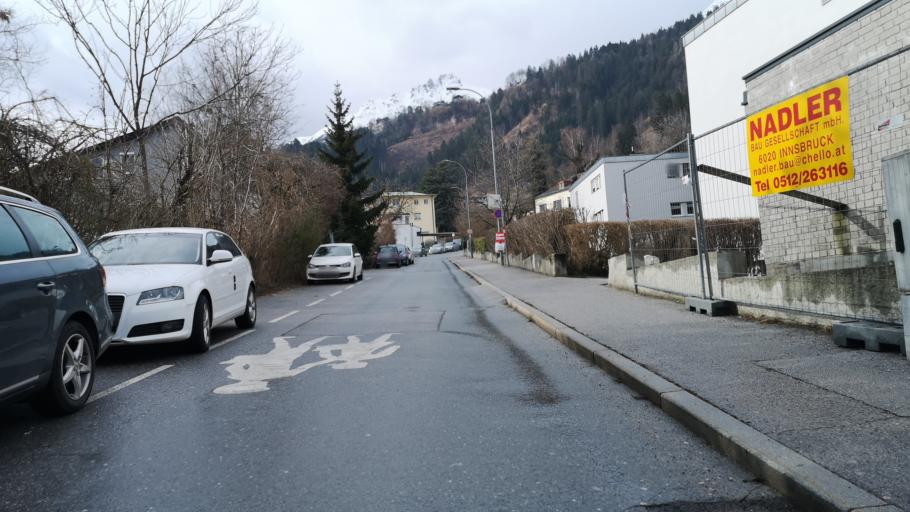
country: AT
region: Tyrol
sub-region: Innsbruck Stadt
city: Innsbruck
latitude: 47.2836
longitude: 11.4119
